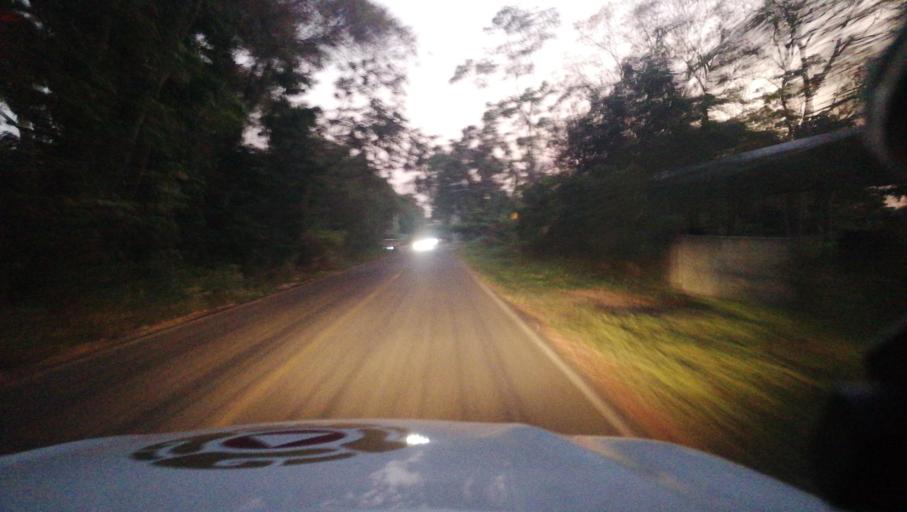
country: MX
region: Chiapas
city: Veinte de Noviembre
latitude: 14.9601
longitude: -92.2541
